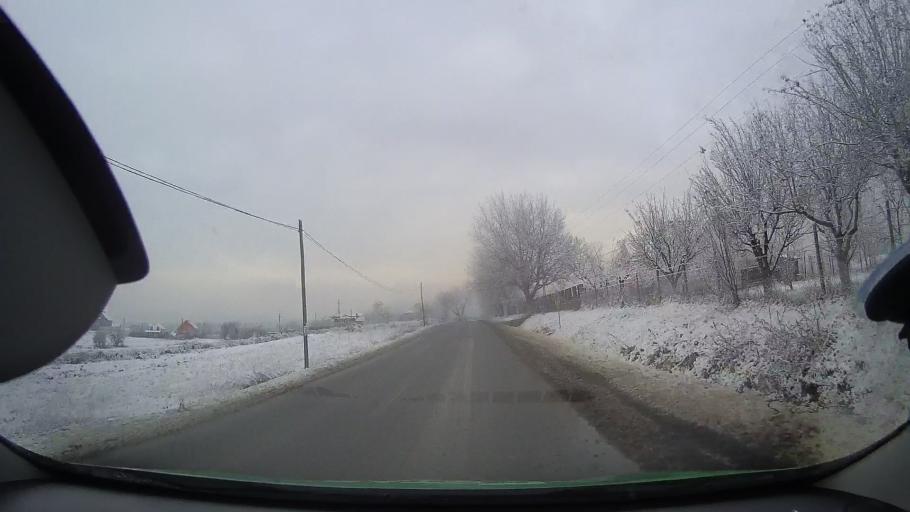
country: RO
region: Mures
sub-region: Comuna Bogata
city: Bogata
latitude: 46.4584
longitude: 24.0801
